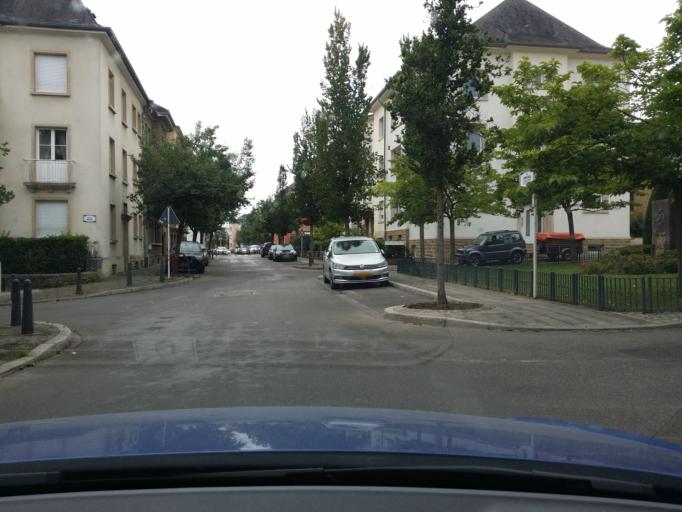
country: LU
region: Luxembourg
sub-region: Canton de Luxembourg
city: Luxembourg
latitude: 49.6227
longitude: 6.1241
